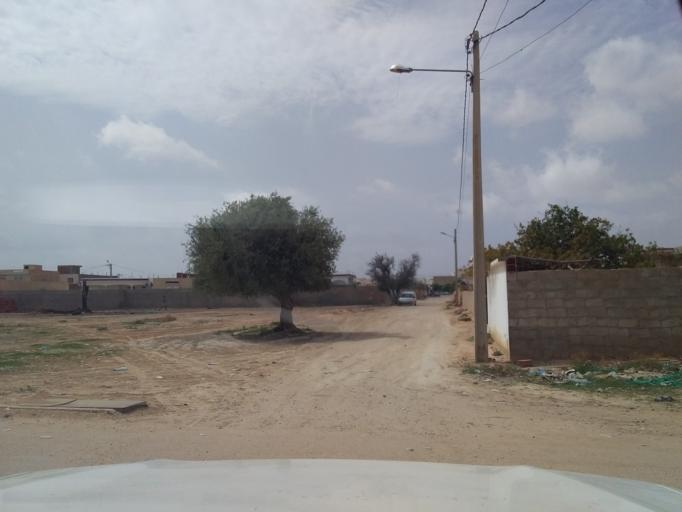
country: TN
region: Qabis
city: Matmata
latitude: 33.6155
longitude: 10.2929
